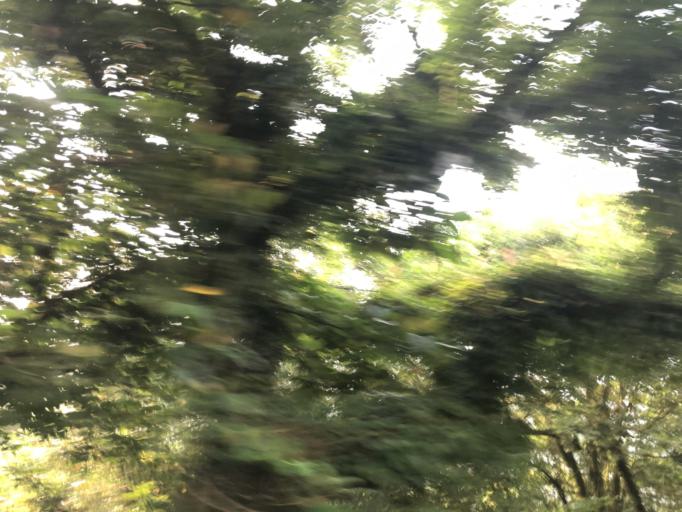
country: TW
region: Taiwan
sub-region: Keelung
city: Keelung
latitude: 25.1496
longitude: 121.6297
